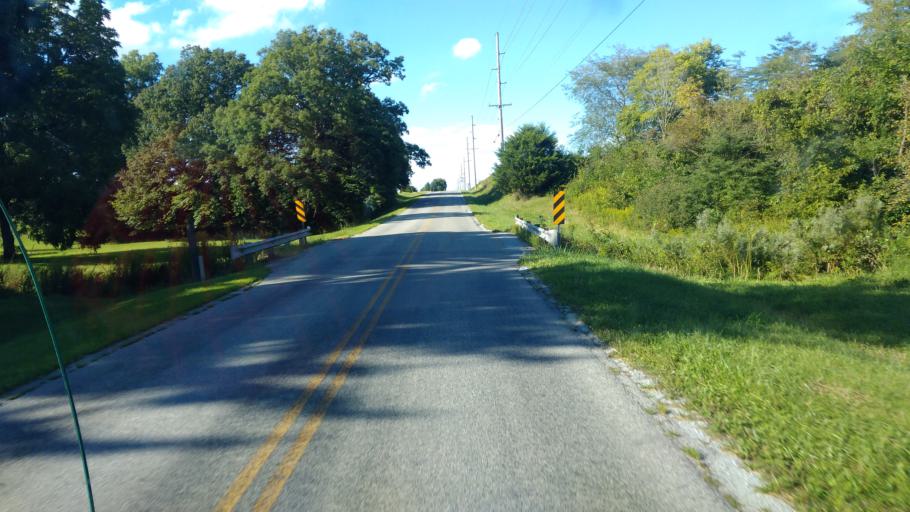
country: US
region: Ohio
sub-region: Hardin County
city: Kenton
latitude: 40.7155
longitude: -83.6533
